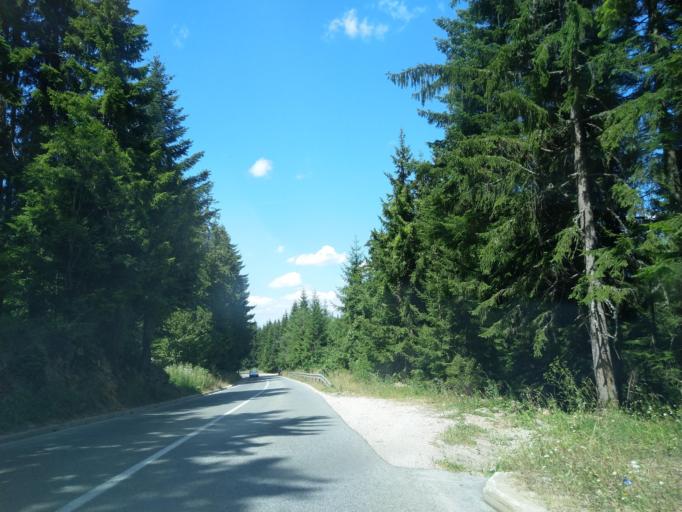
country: RS
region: Central Serbia
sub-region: Zlatiborski Okrug
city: Nova Varos
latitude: 43.4099
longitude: 19.8377
